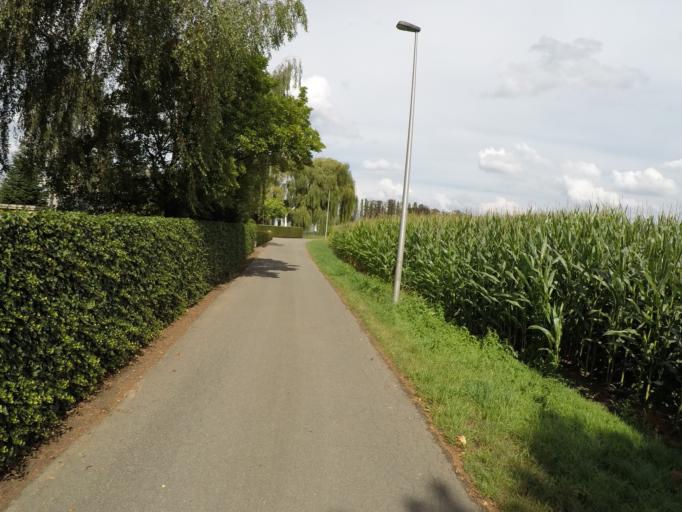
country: BE
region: Flanders
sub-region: Provincie Antwerpen
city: Ranst
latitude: 51.1680
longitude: 4.5589
